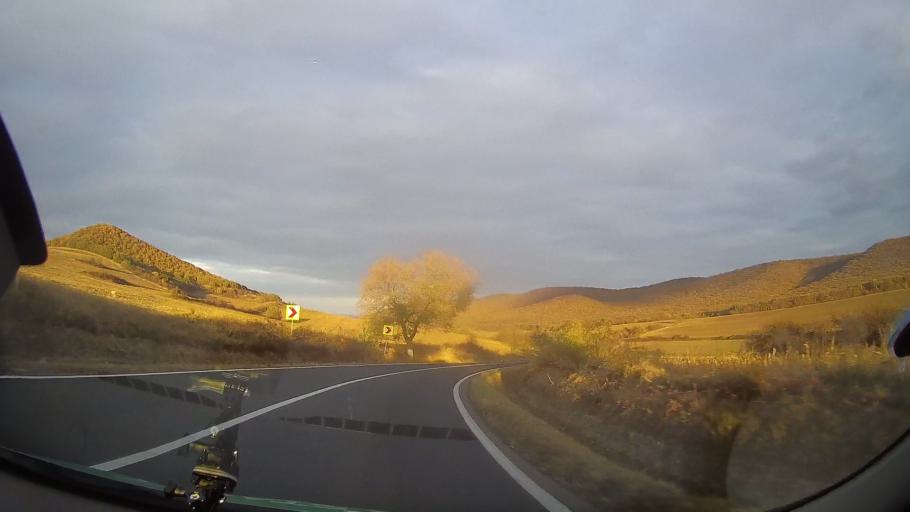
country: RO
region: Tulcea
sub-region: Comuna Ciucurova
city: Ciucurova
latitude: 44.9457
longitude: 28.4973
